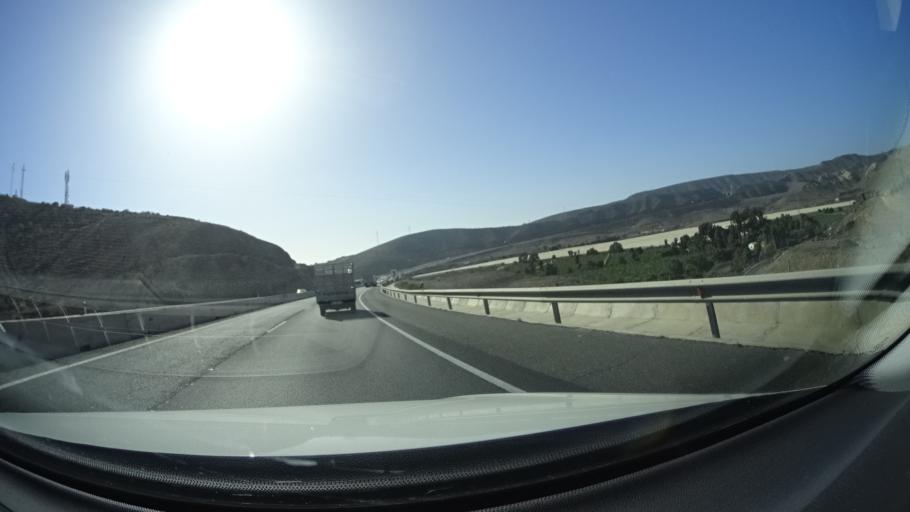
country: ES
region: Canary Islands
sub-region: Provincia de Las Palmas
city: Puerto Rico
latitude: 27.7686
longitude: -15.6645
